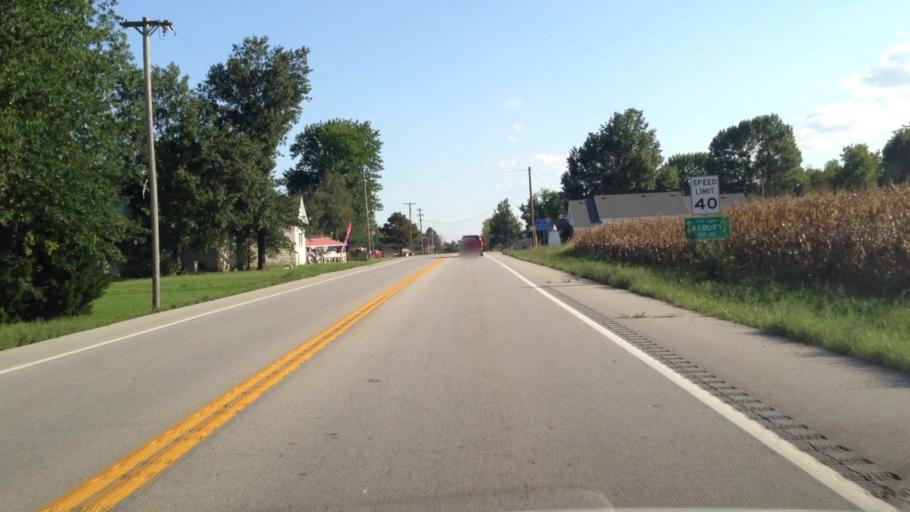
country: US
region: Missouri
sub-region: Jasper County
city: Carl Junction
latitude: 37.2770
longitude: -94.6010
